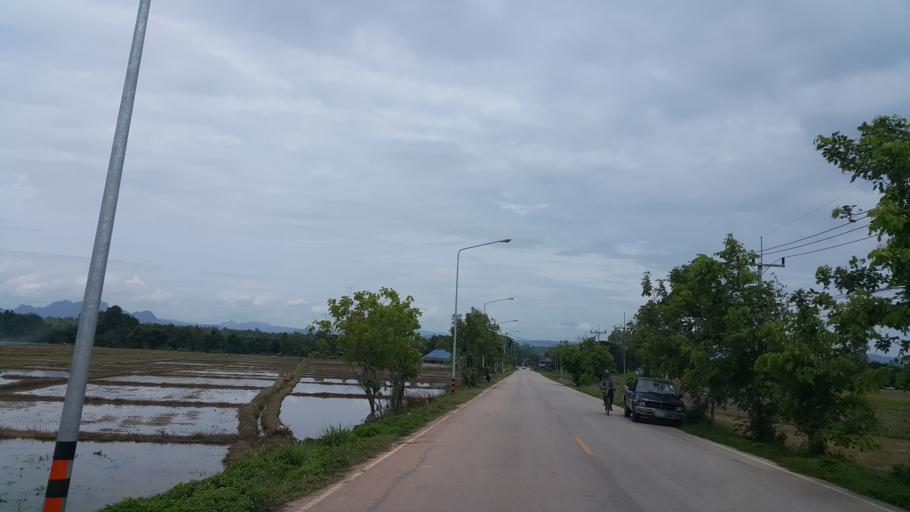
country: TH
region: Lampang
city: Chae Hom
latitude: 18.7607
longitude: 99.5584
